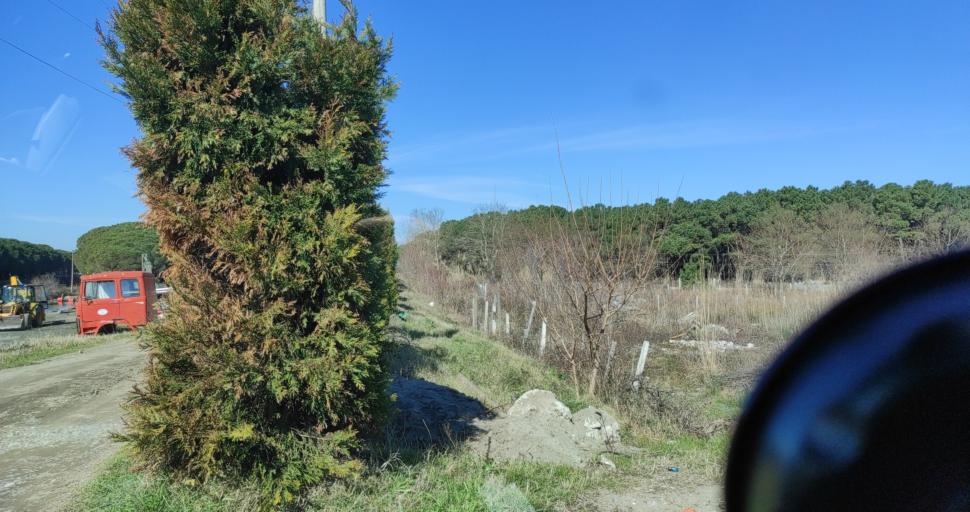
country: AL
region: Shkoder
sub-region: Rrethi i Shkodres
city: Velipoje
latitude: 41.8614
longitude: 19.4464
